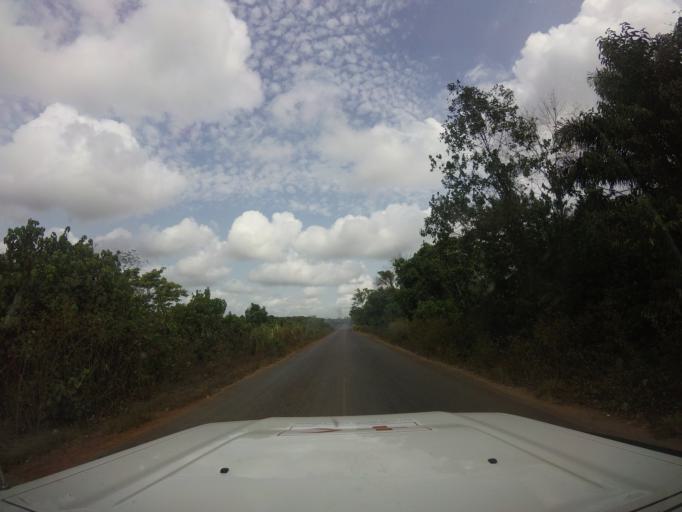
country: LR
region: Bomi
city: Tubmanburg
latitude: 6.7263
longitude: -10.9860
